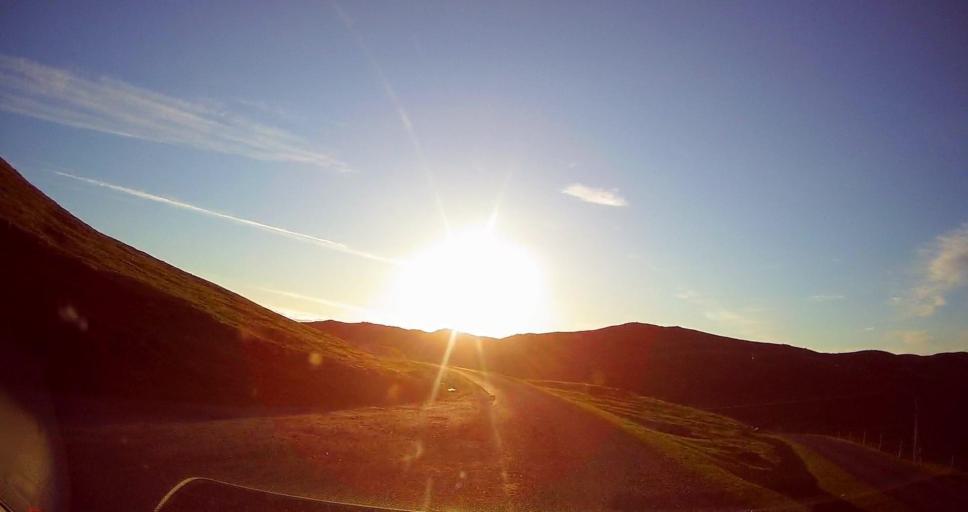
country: GB
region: Scotland
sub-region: Shetland Islands
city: Lerwick
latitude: 60.4483
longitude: -1.4165
